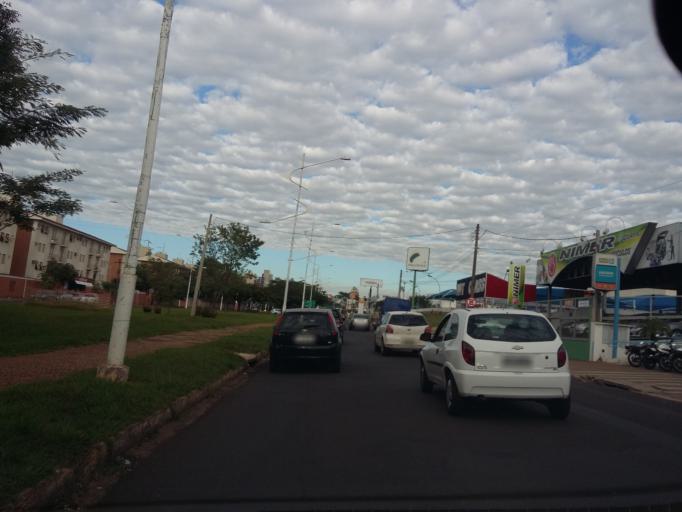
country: BR
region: Sao Paulo
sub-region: Sao Jose Do Rio Preto
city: Sao Jose do Rio Preto
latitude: -20.8217
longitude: -49.3997
